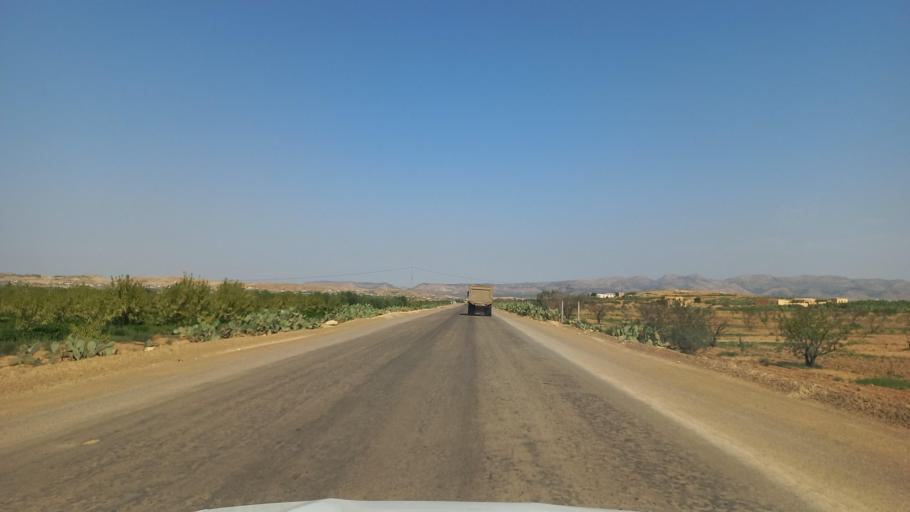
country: TN
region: Al Qasrayn
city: Sbiba
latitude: 35.3579
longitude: 9.0470
